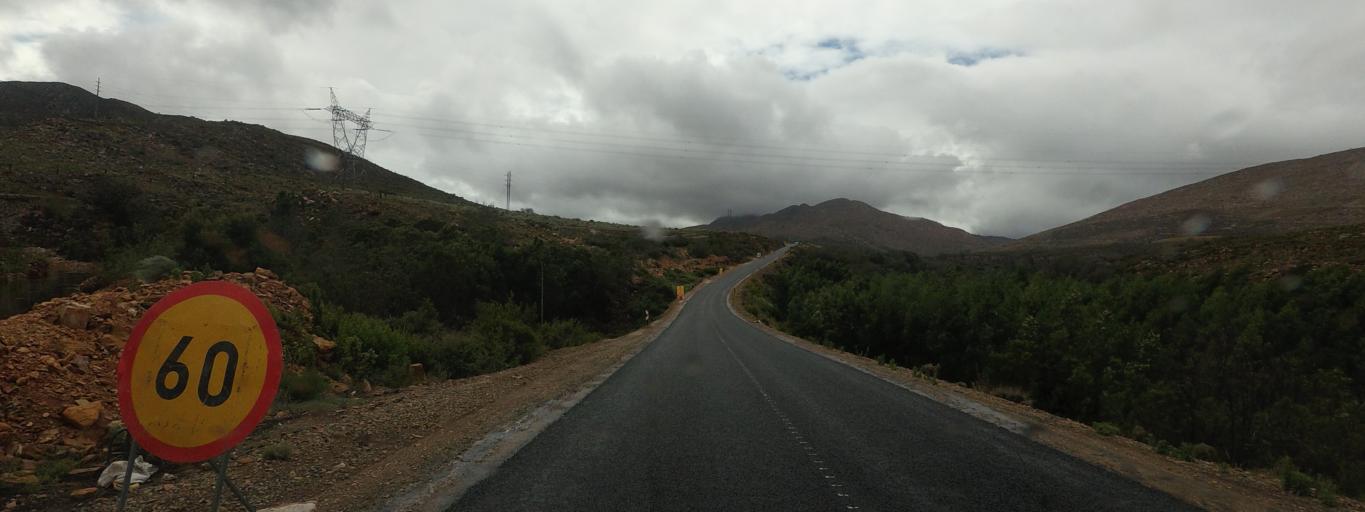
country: ZA
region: Western Cape
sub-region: Eden District Municipality
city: George
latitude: -33.8061
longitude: 22.3360
